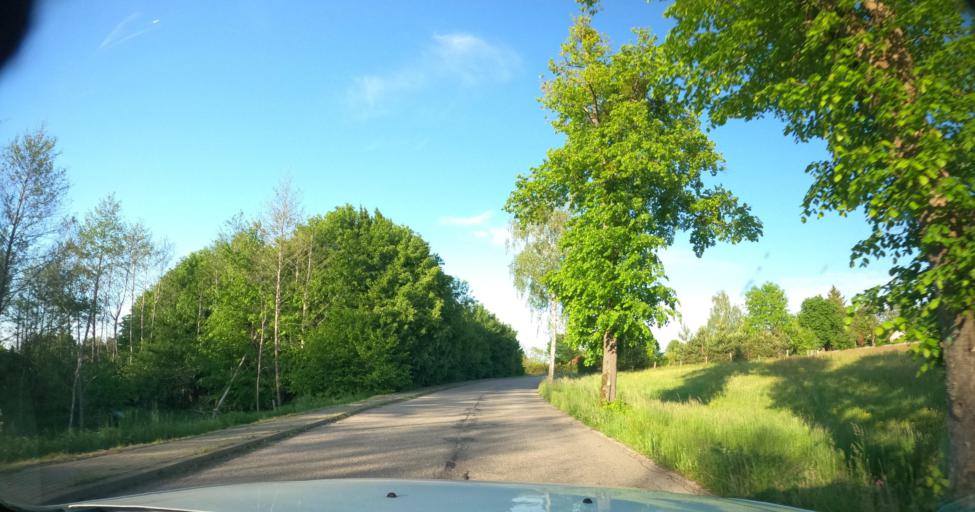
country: PL
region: Warmian-Masurian Voivodeship
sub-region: Powiat braniewski
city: Pieniezno
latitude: 54.2559
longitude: 19.9897
